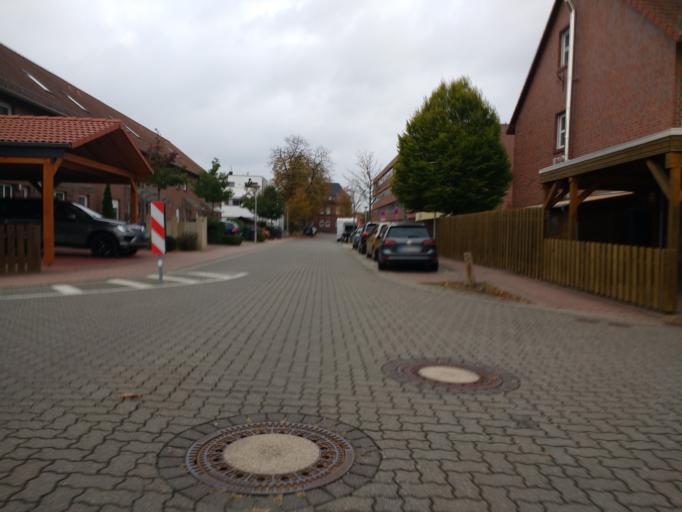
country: DE
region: Lower Saxony
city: Weyhausen
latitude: 52.4222
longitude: 10.7188
